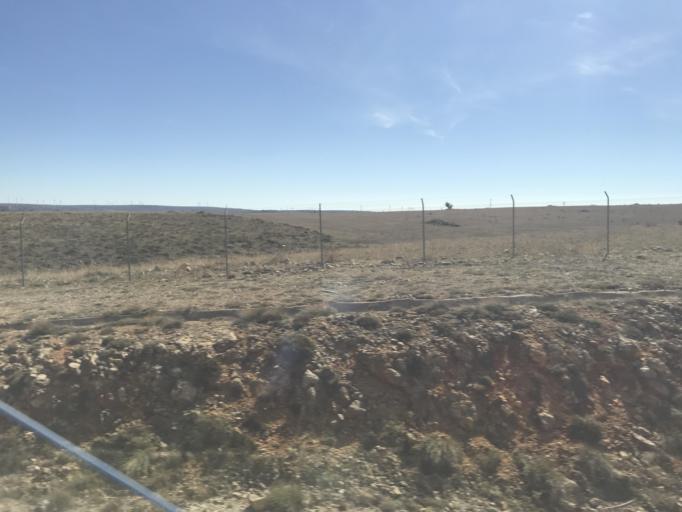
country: ES
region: Castille-La Mancha
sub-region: Provincia de Guadalajara
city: Anguita
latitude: 41.1150
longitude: -2.3568
